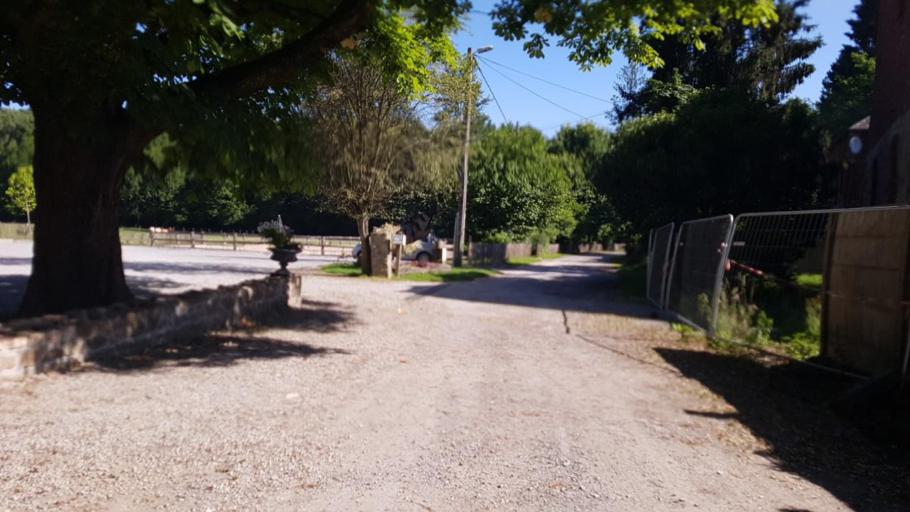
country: FR
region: Nord-Pas-de-Calais
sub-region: Departement du Nord
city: Anor
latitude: 49.9734
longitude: 4.1209
